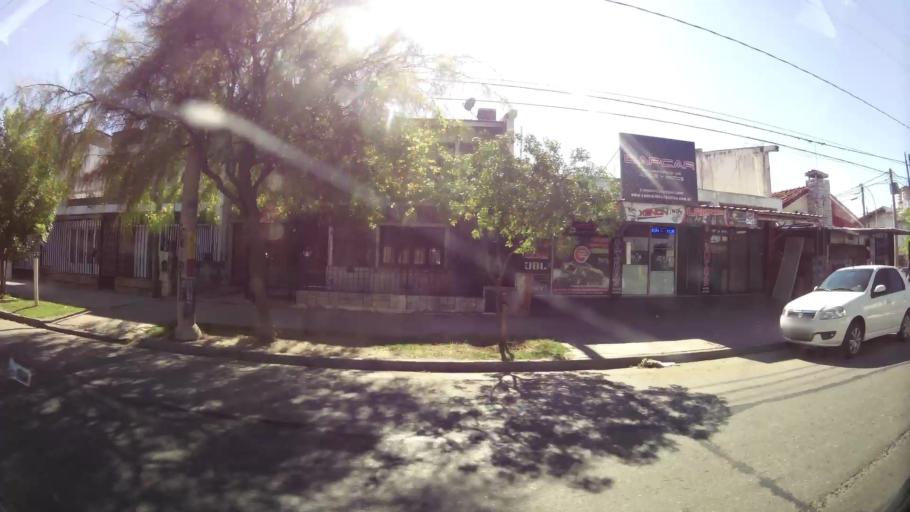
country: AR
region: Cordoba
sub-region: Departamento de Capital
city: Cordoba
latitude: -31.4360
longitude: -64.1688
